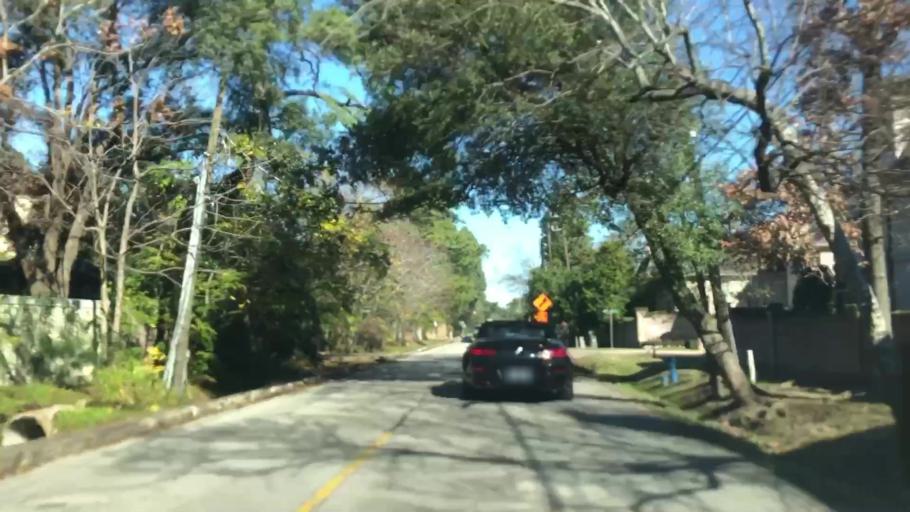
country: US
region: Texas
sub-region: Harris County
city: Hunters Creek Village
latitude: 29.7591
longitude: -95.4676
